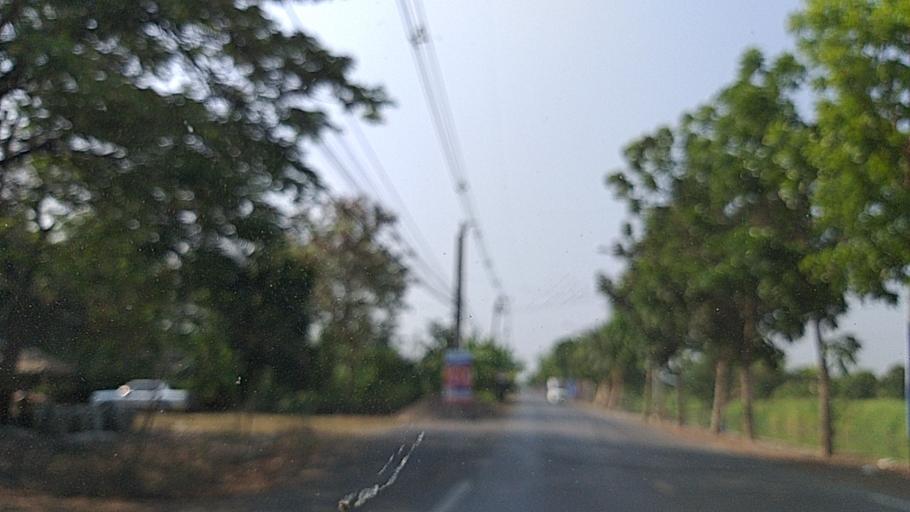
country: TH
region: Pathum Thani
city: Lam Luk Ka
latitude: 13.9690
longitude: 100.7066
